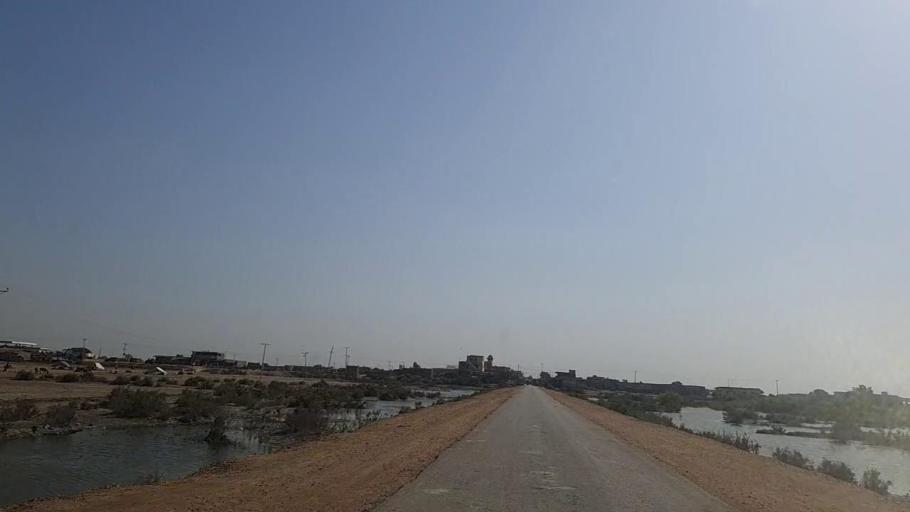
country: PK
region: Sindh
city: Mirpur Batoro
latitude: 24.6212
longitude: 68.2950
